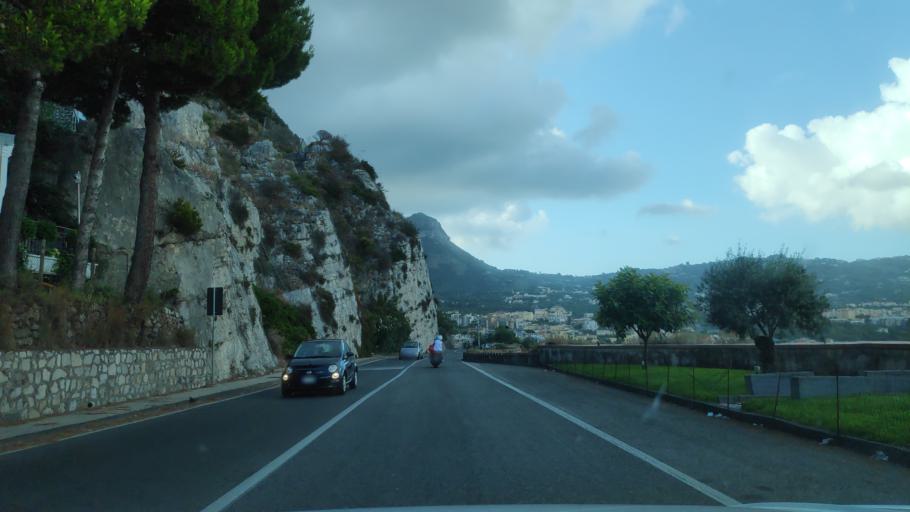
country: IT
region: Campania
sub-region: Provincia di Napoli
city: Meta
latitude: 40.6476
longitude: 14.4123
